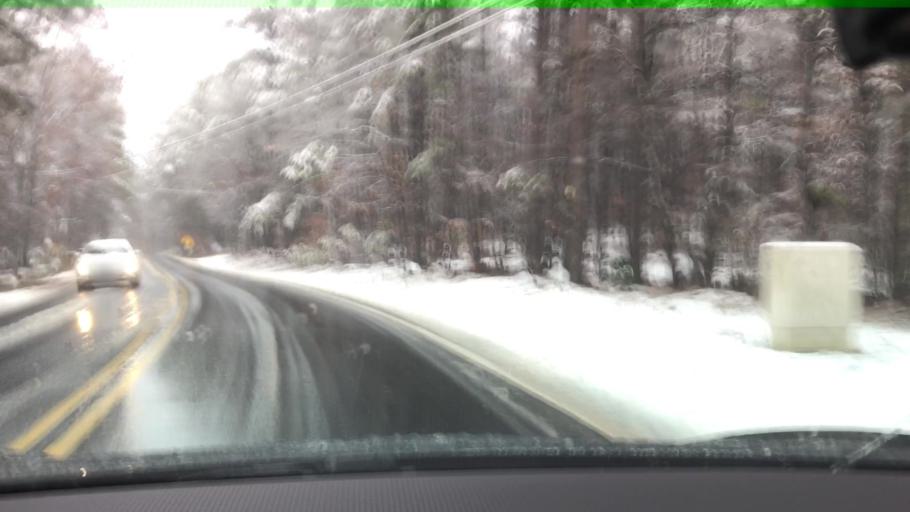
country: US
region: Georgia
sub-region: Gwinnett County
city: Suwanee
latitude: 34.0186
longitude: -84.0742
